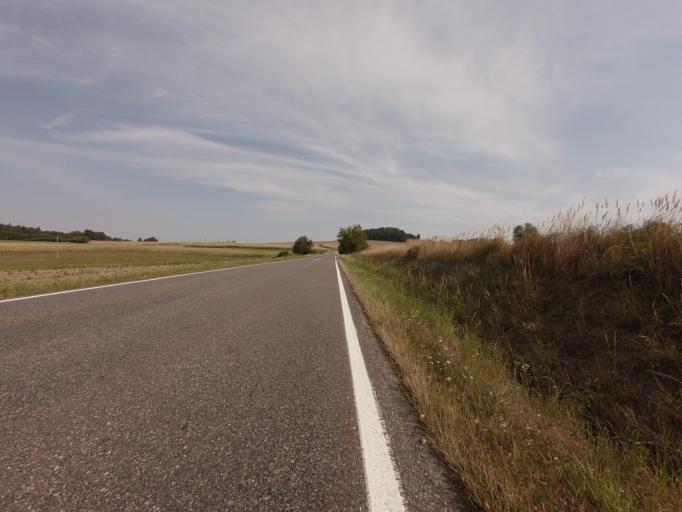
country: CZ
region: Jihocesky
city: Milevsko
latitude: 49.5048
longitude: 14.3636
